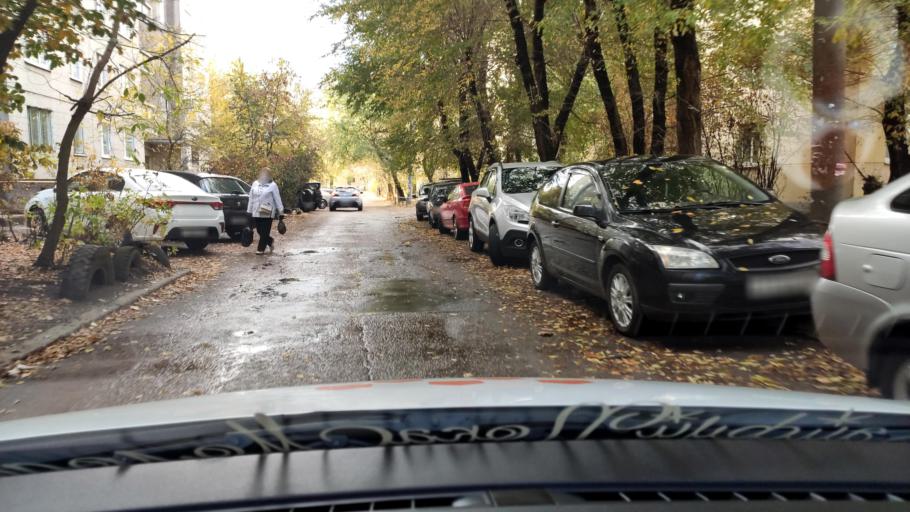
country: RU
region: Voronezj
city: Voronezh
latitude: 51.6494
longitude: 39.1324
